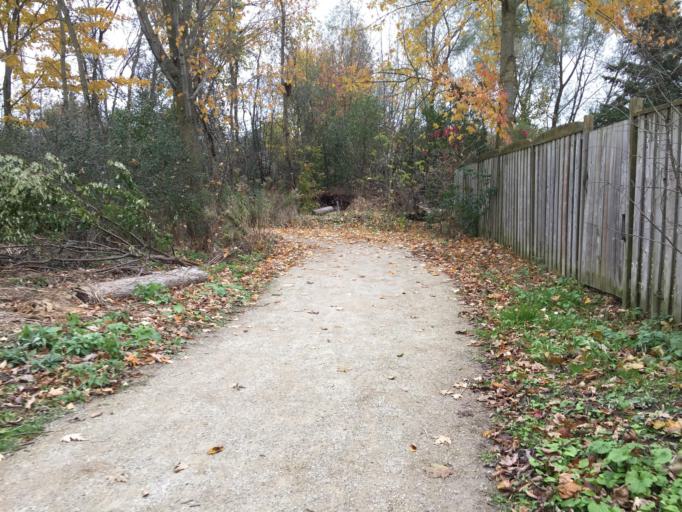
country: CA
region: Ontario
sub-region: Wellington County
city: Guelph
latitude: 43.5238
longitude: -80.3028
